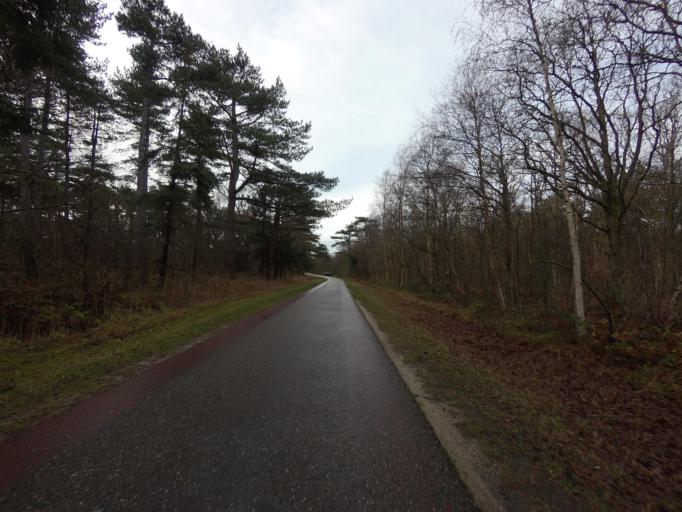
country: NL
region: North Holland
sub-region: Gemeente Texel
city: Den Burg
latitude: 53.0495
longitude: 4.7305
